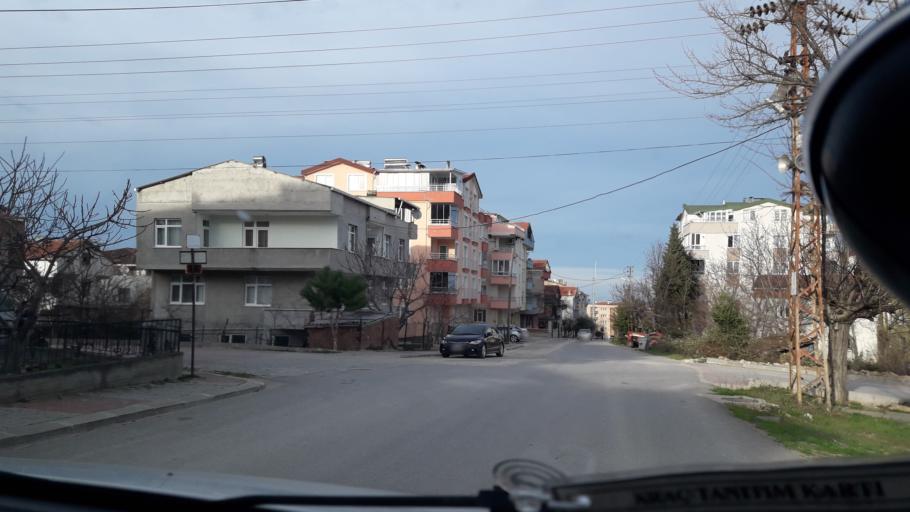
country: TR
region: Sinop
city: Gerze
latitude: 41.8052
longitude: 35.1849
